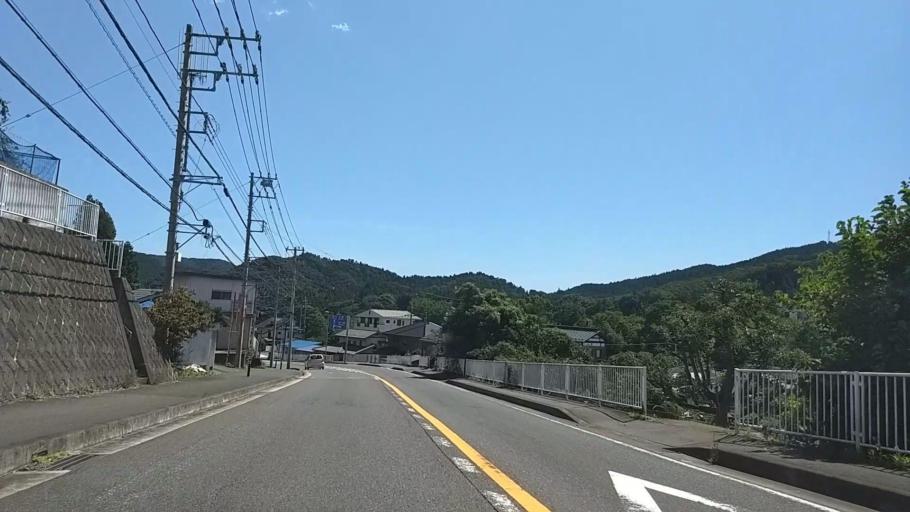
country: JP
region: Tokyo
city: Hachioji
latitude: 35.5669
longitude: 139.2441
